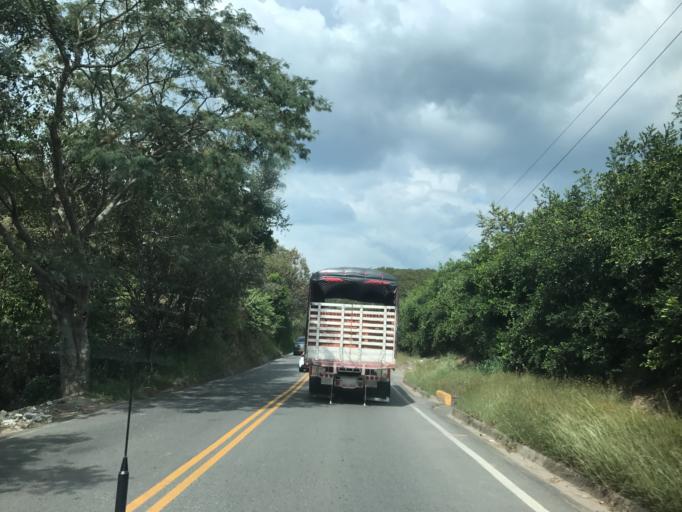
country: CO
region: Valle del Cauca
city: Cartago
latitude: 4.7375
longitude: -75.8985
